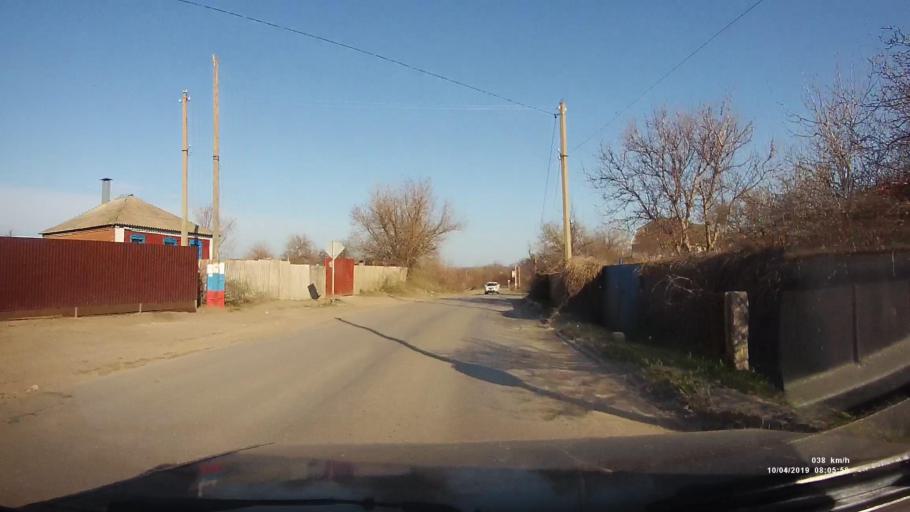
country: RU
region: Rostov
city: Staraya Stanitsa
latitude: 48.3363
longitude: 40.2948
